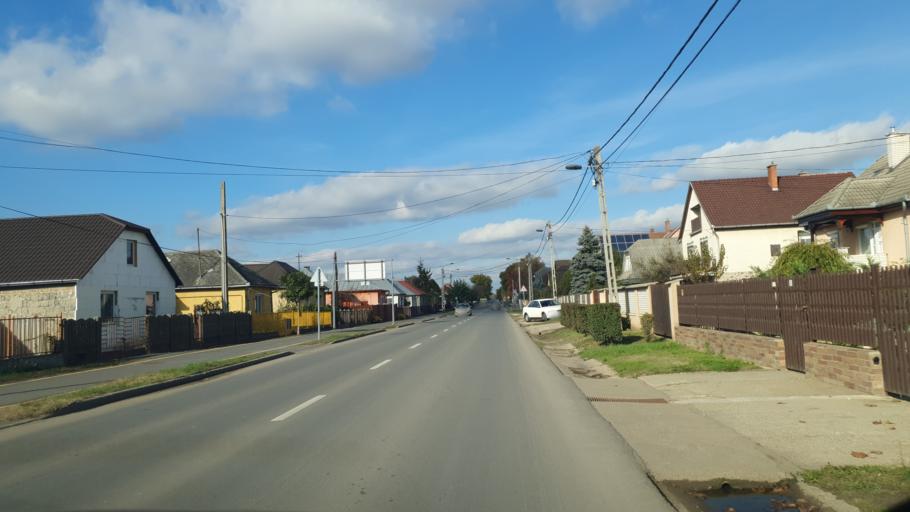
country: HU
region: Szabolcs-Szatmar-Bereg
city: Kisvarda
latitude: 48.2036
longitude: 22.0909
